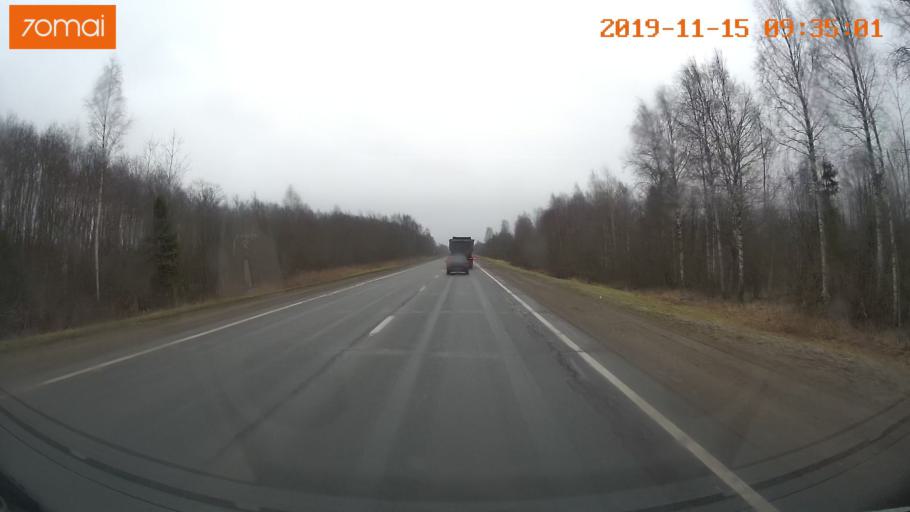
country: RU
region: Vologda
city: Sheksna
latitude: 59.2566
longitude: 38.3913
